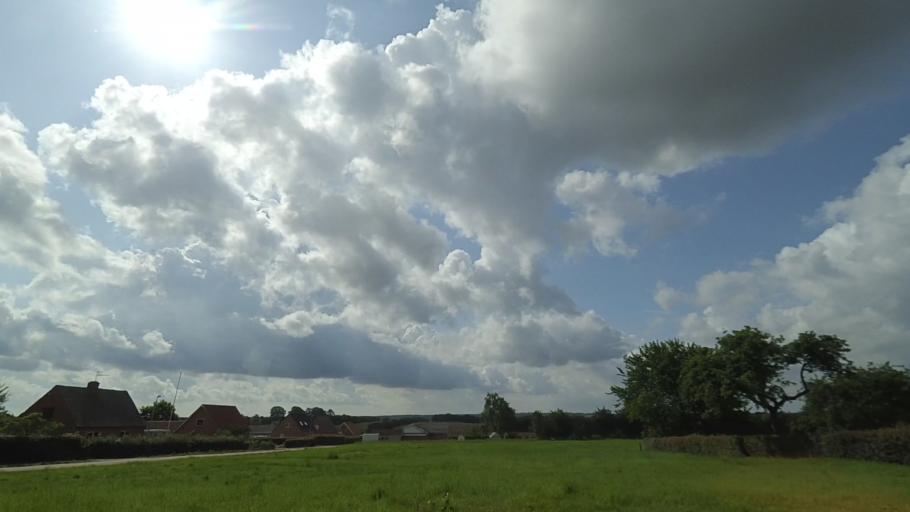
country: DK
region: Central Jutland
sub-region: Norddjurs Kommune
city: Auning
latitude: 56.4827
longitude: 10.4400
